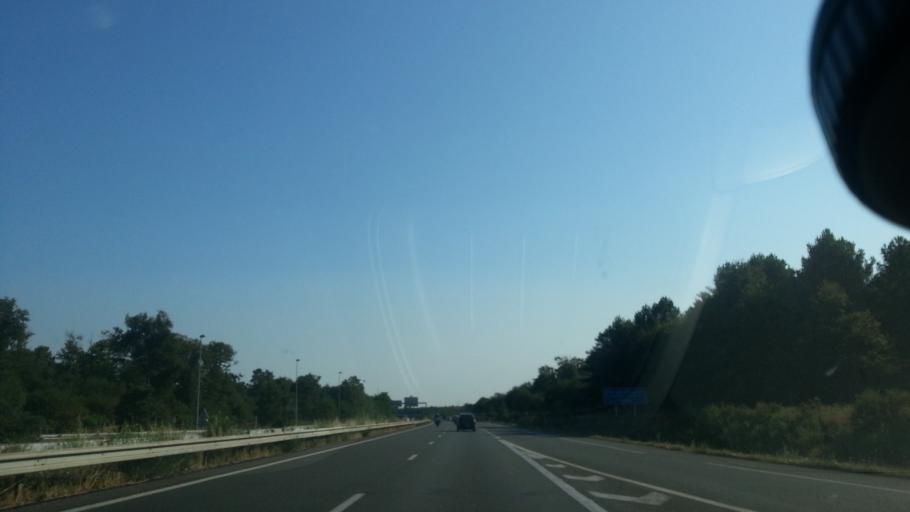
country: FR
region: Poitou-Charentes
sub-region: Departement de la Vienne
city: Naintre
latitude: 46.7820
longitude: 0.5015
